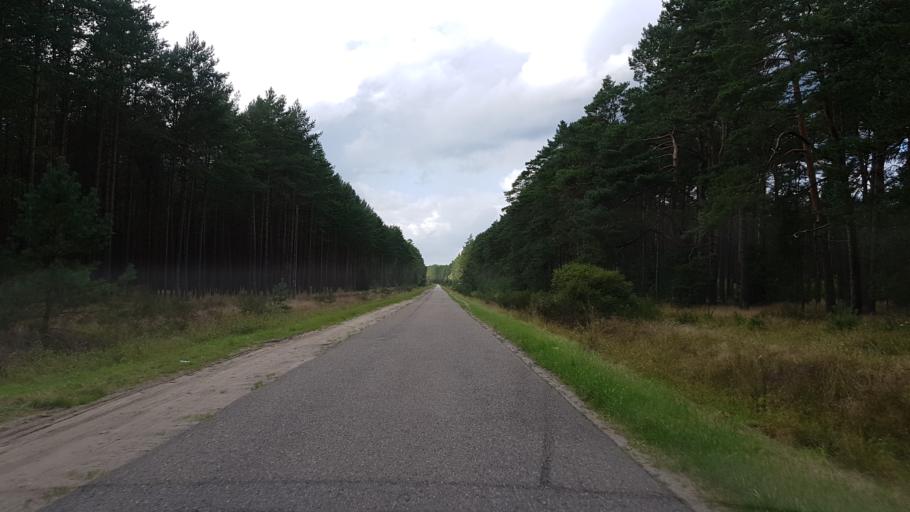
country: PL
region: West Pomeranian Voivodeship
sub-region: Powiat bialogardzki
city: Tychowo
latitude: 54.0357
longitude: 16.3386
